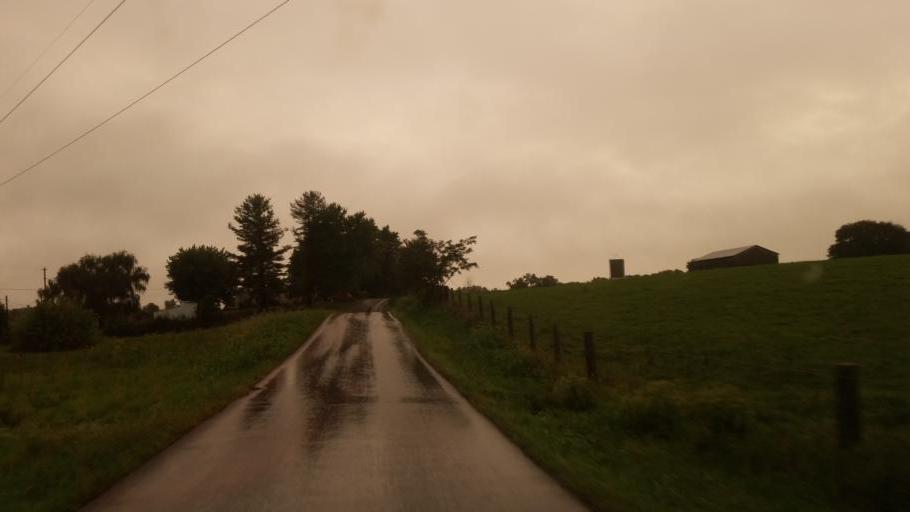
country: US
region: Kentucky
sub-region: Fleming County
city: Flemingsburg
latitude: 38.4693
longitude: -83.6379
